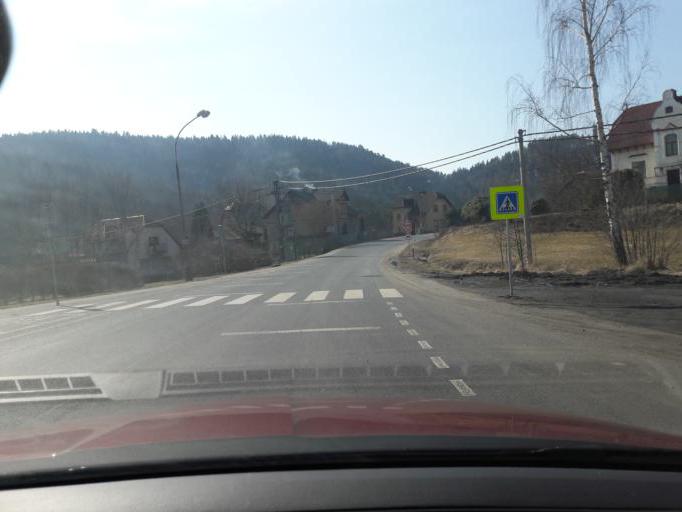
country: CZ
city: Novy Bor
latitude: 50.7387
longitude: 14.5874
